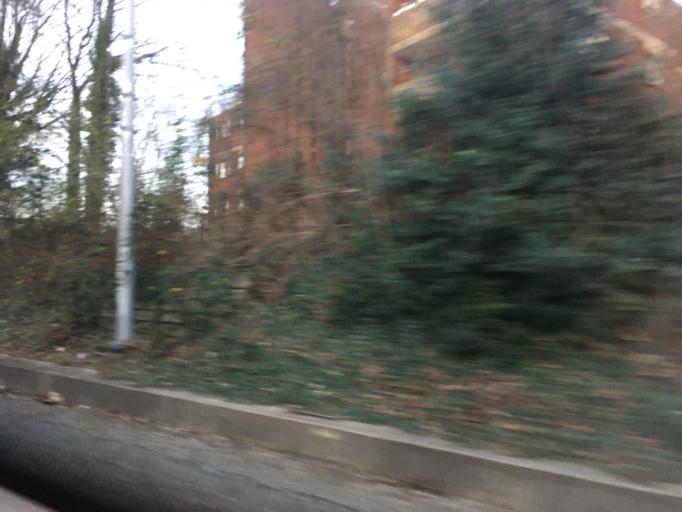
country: GB
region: England
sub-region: Manchester
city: Chorlton cum Hardy
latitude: 53.4418
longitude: -2.2722
